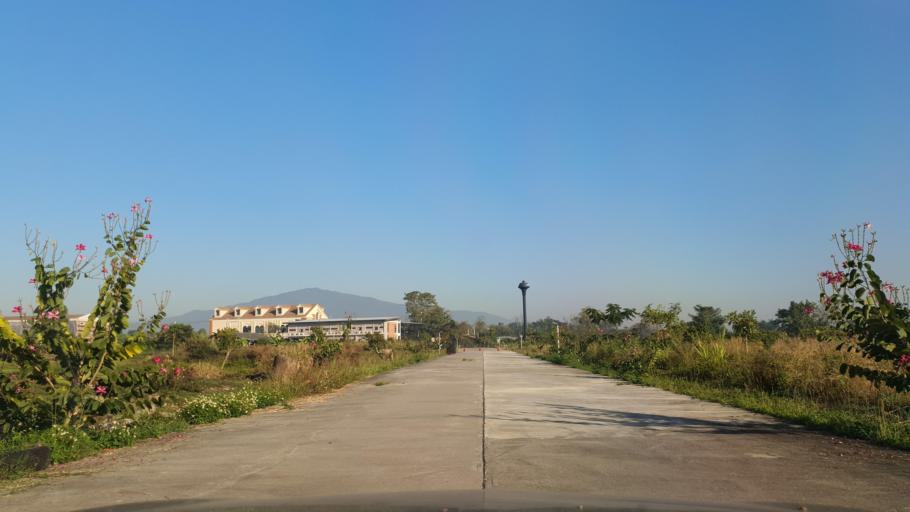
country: TH
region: Chiang Mai
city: Hang Dong
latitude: 18.6943
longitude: 98.9680
